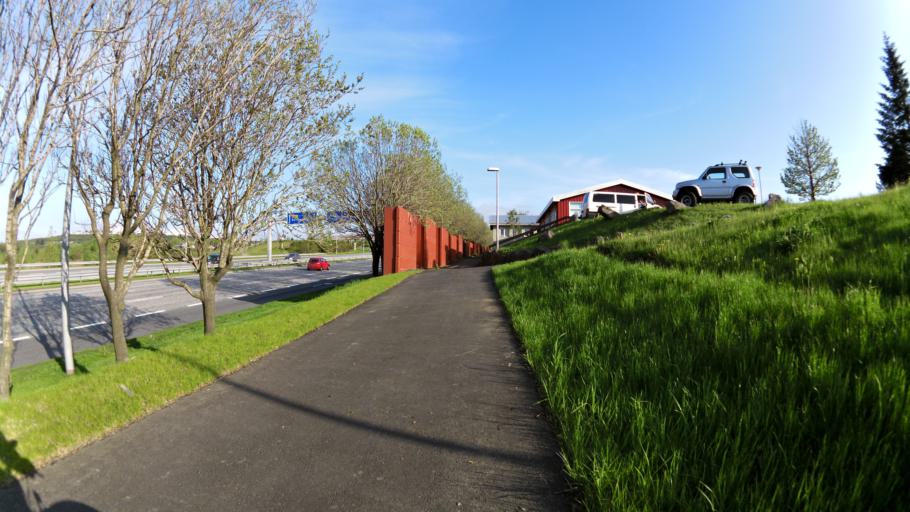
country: IS
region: Capital Region
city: Reykjavik
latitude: 64.1168
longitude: -21.8448
